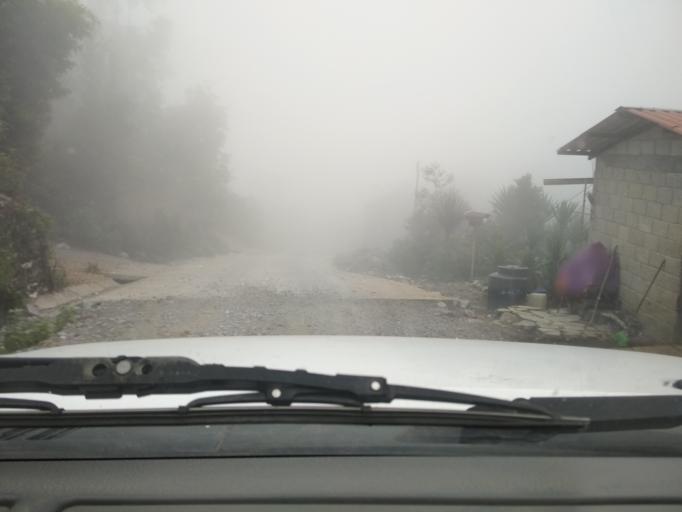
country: MX
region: Veracruz
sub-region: La Perla
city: Barrio de San Miguel
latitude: 18.9454
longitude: -97.1210
